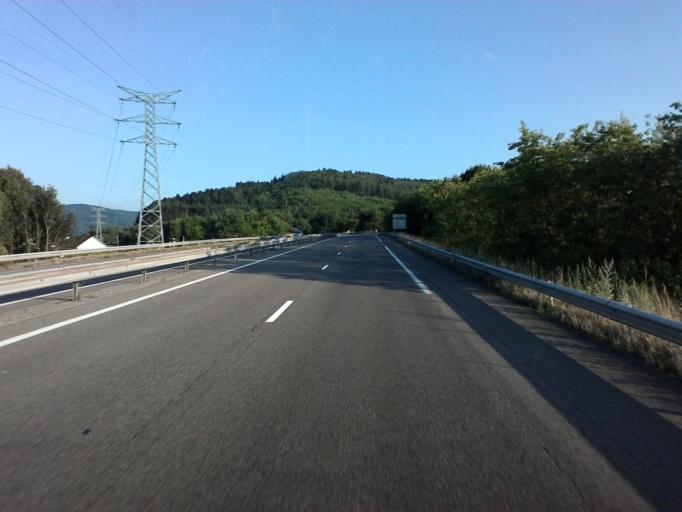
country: FR
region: Lorraine
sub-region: Departement des Vosges
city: Eloyes
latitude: 48.0983
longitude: 6.5897
